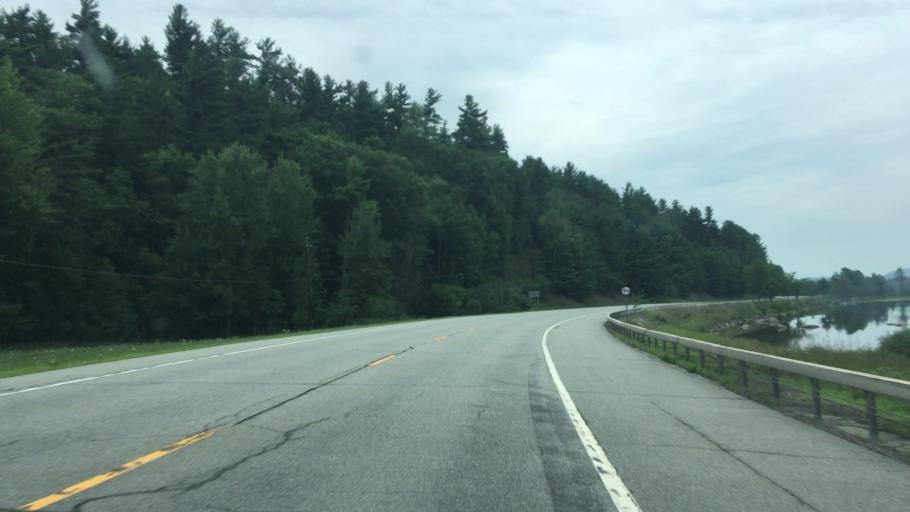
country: US
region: New York
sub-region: Essex County
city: Elizabethtown
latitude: 44.3528
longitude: -73.7546
